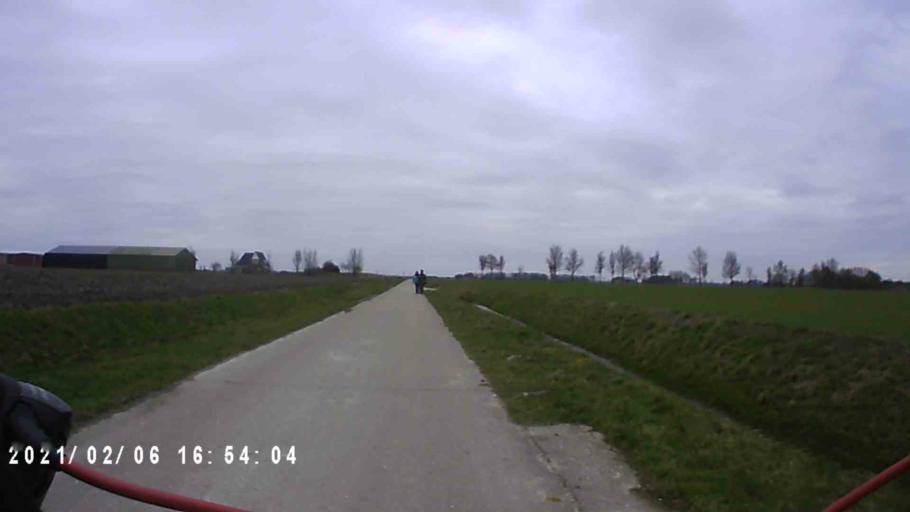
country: NL
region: Groningen
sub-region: Gemeente Appingedam
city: Appingedam
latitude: 53.4116
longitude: 6.7503
